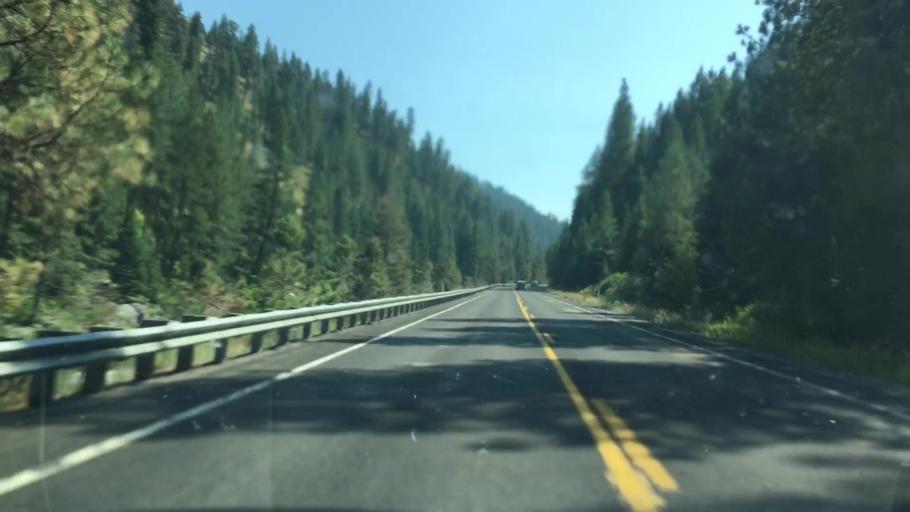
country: US
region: Idaho
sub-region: Valley County
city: Cascade
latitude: 44.2418
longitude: -116.1030
